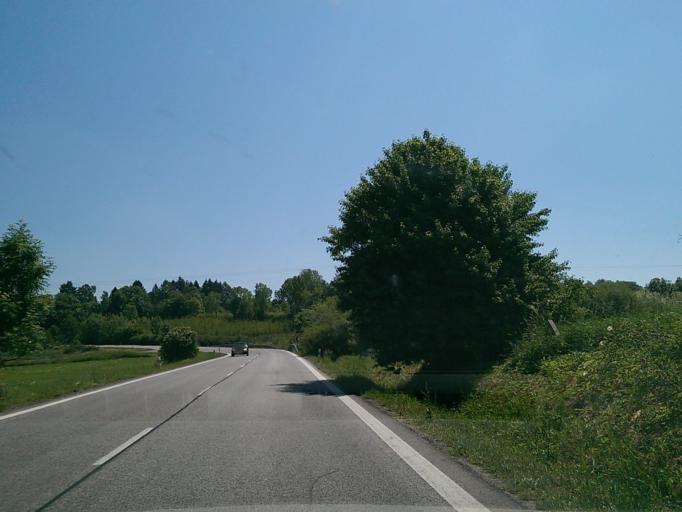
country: CZ
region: Kralovehradecky
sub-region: Okres Jicin
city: Jicin
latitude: 50.4937
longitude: 15.3142
